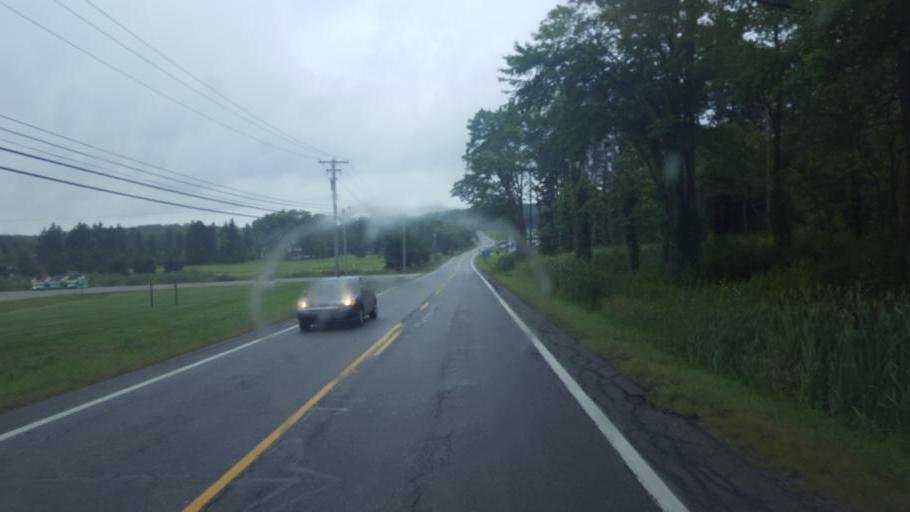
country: US
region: Ohio
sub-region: Geauga County
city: Burton
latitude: 41.5280
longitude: -81.1936
